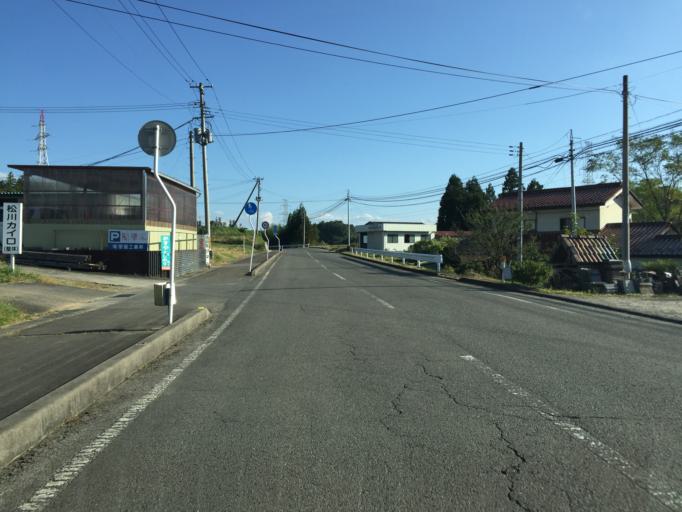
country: JP
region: Fukushima
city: Nihommatsu
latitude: 37.6482
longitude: 140.4916
